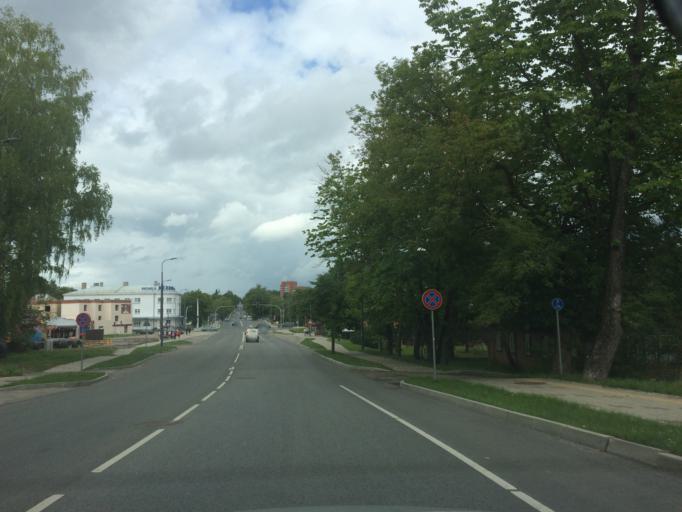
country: LV
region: Rezekne
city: Rezekne
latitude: 56.4986
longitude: 27.3267
